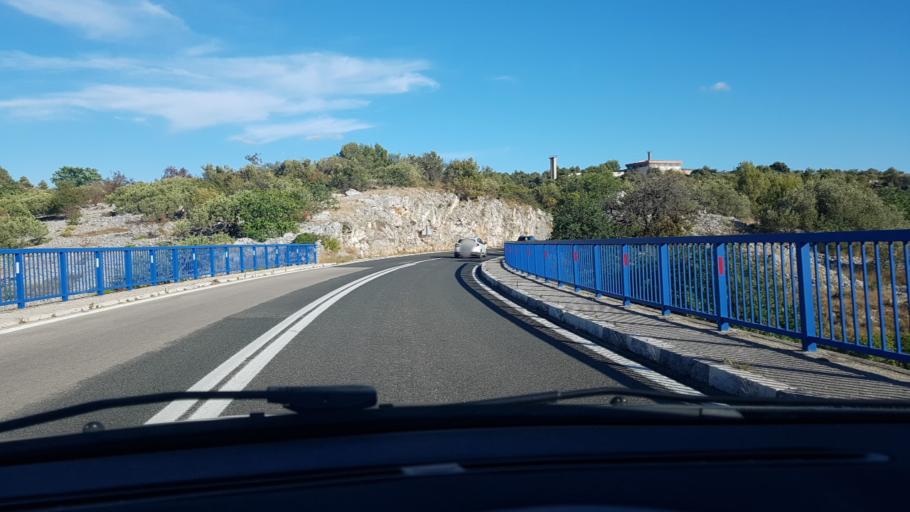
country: HR
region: Sibensko-Kniniska
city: Primosten
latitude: 43.5869
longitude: 15.9352
